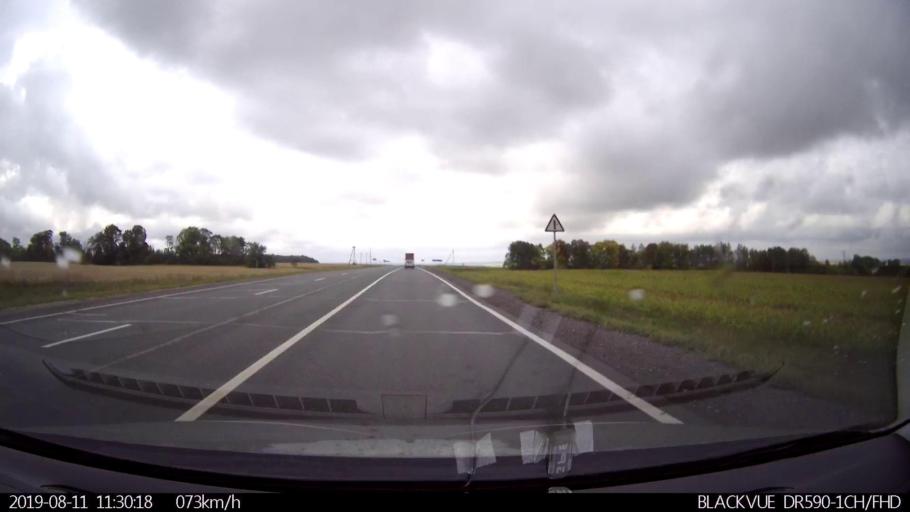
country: RU
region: Ulyanovsk
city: Krasnyy Gulyay
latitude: 54.0601
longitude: 48.2198
